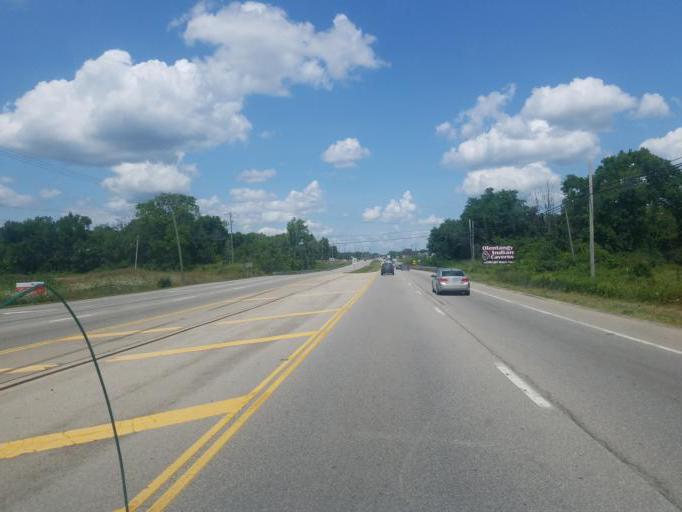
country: US
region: Ohio
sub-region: Delaware County
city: Lewis Center
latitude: 40.1950
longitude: -83.0274
